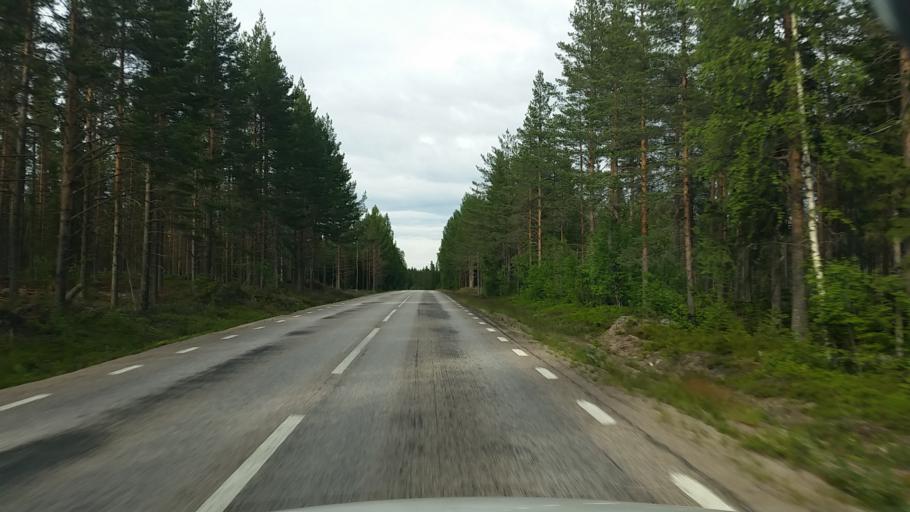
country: SE
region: Gaevleborg
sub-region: Ljusdals Kommun
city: Farila
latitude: 61.9816
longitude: 15.1300
